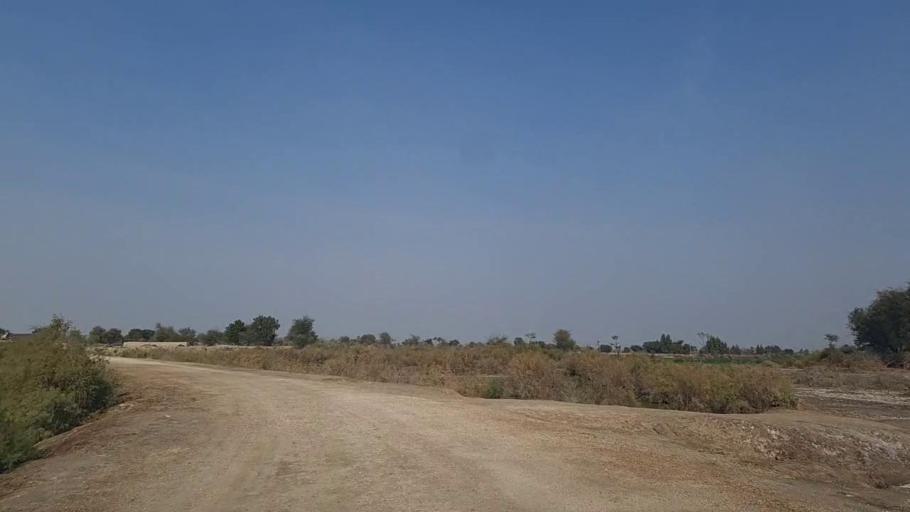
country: PK
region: Sindh
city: Daur
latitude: 26.5128
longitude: 68.4814
